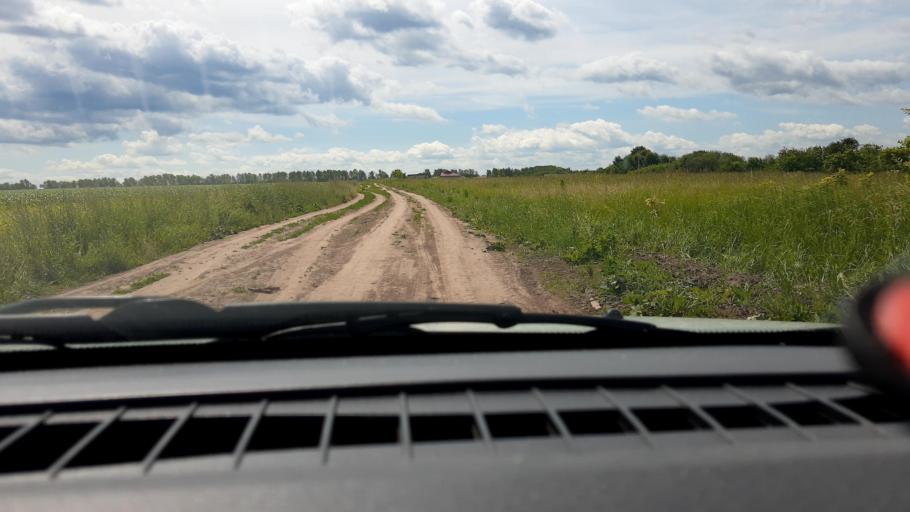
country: RU
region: Nizjnij Novgorod
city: Afonino
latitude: 56.1269
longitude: 44.0321
